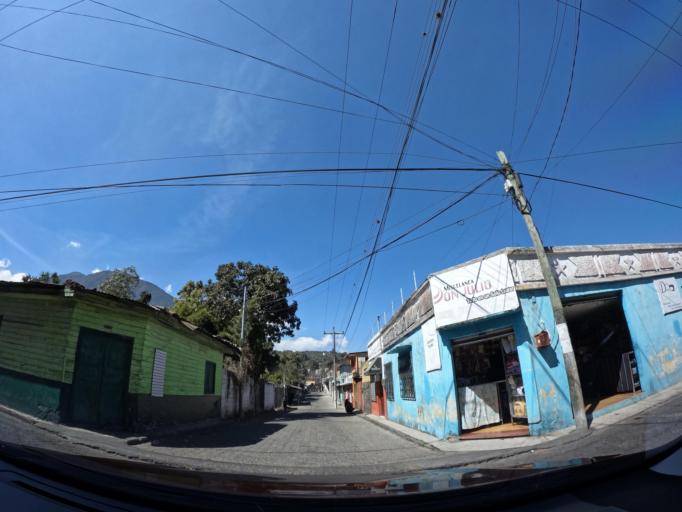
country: GT
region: Solola
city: San Lucas Toliman
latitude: 14.6362
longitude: -91.1434
